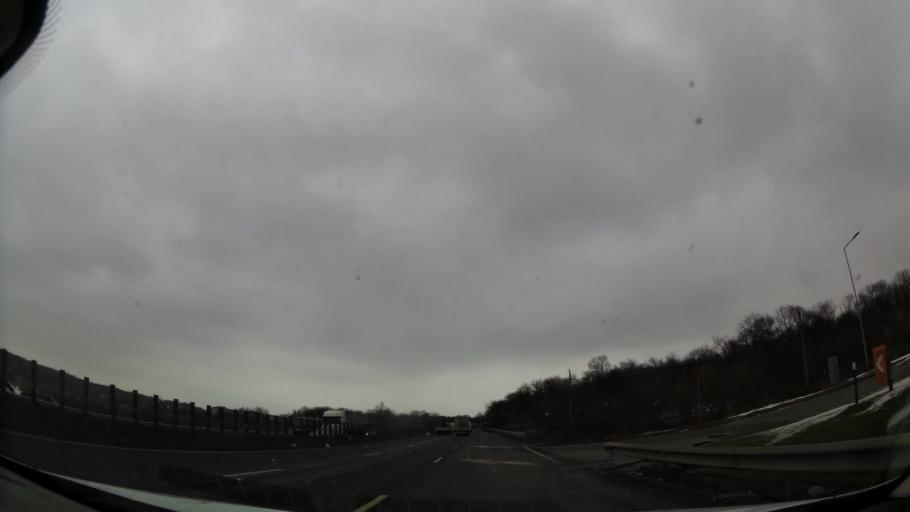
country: RO
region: Ilfov
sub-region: Comuna Mogosoaia
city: Mogosoaia
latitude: 44.5102
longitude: 26.0079
